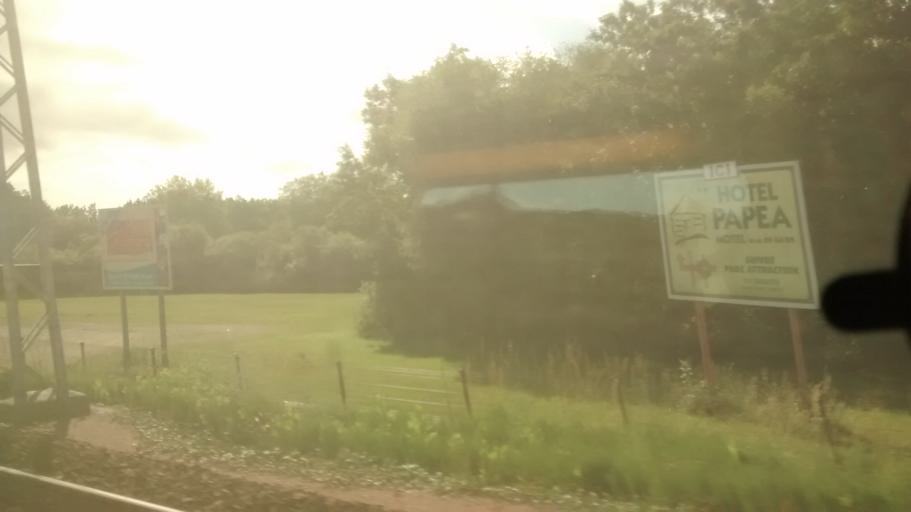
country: FR
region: Pays de la Loire
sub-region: Departement de la Sarthe
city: Sarge-les-le-Mans
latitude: 48.0013
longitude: 0.2466
